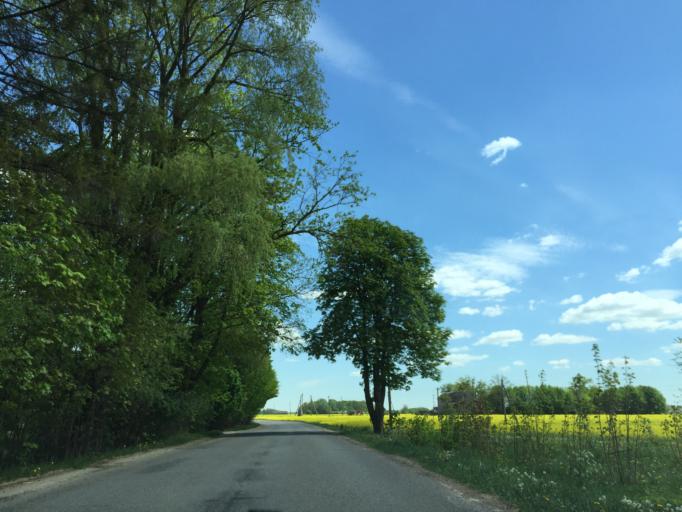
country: LV
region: Bauskas Rajons
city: Bauska
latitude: 56.4096
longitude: 24.1296
